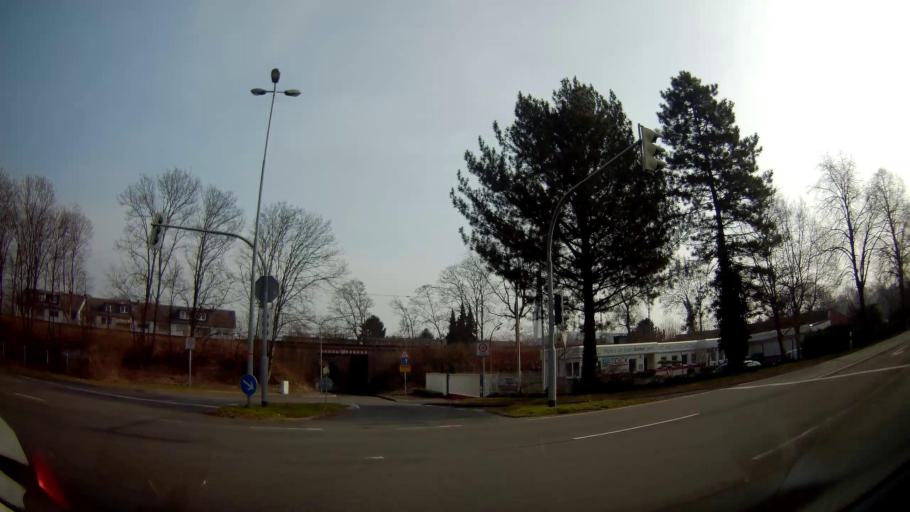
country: DE
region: North Rhine-Westphalia
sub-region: Regierungsbezirk Dusseldorf
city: Moers
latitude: 51.4858
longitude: 6.6330
